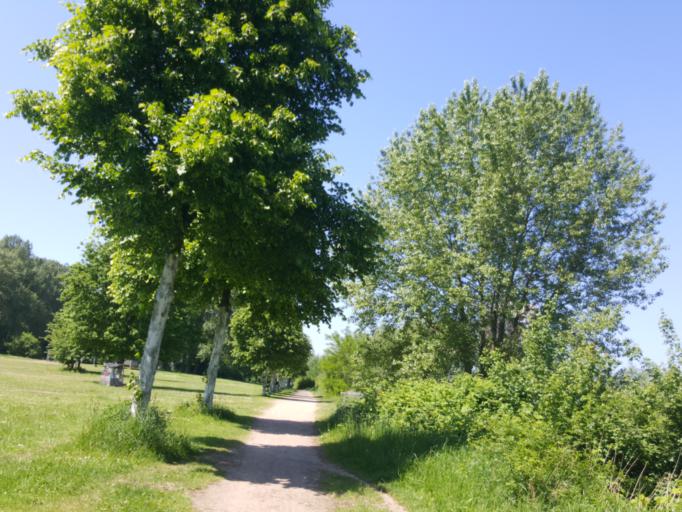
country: DE
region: Hamburg
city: Rothenburgsort
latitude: 53.5323
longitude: 10.0344
